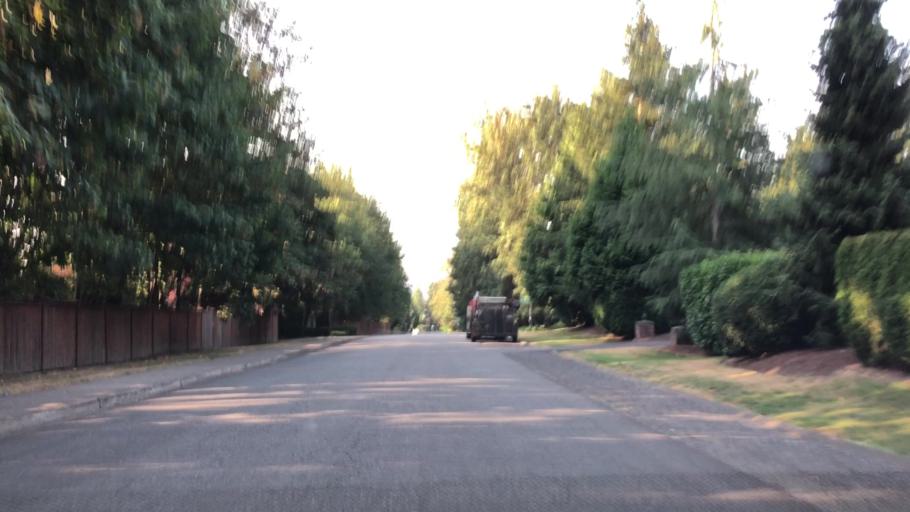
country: US
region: Washington
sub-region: King County
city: Cottage Lake
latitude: 47.7209
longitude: -122.1021
